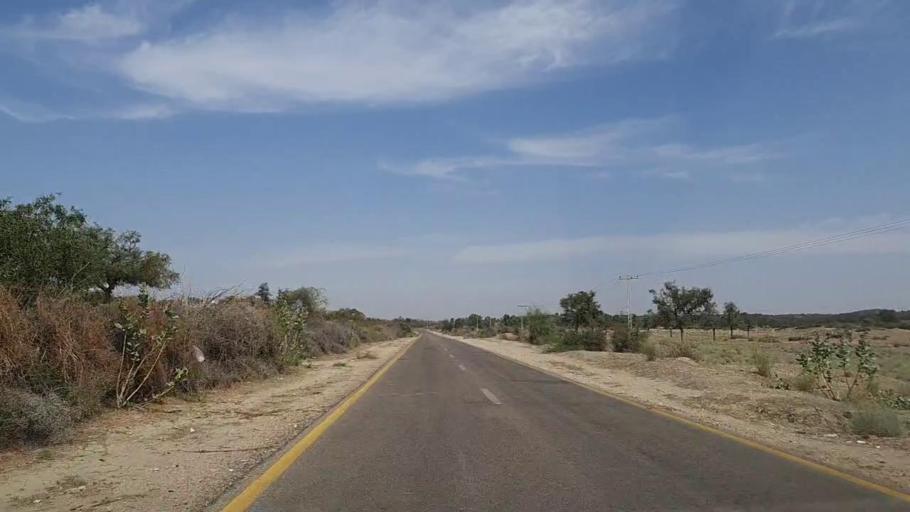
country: PK
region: Sindh
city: Mithi
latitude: 24.7905
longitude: 69.8136
